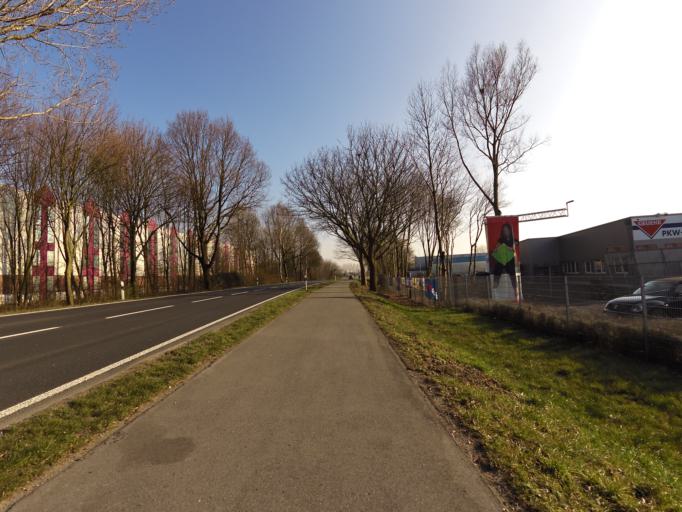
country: DE
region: North Rhine-Westphalia
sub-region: Regierungsbezirk Dusseldorf
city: Emmerich
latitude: 51.8406
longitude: 6.2752
